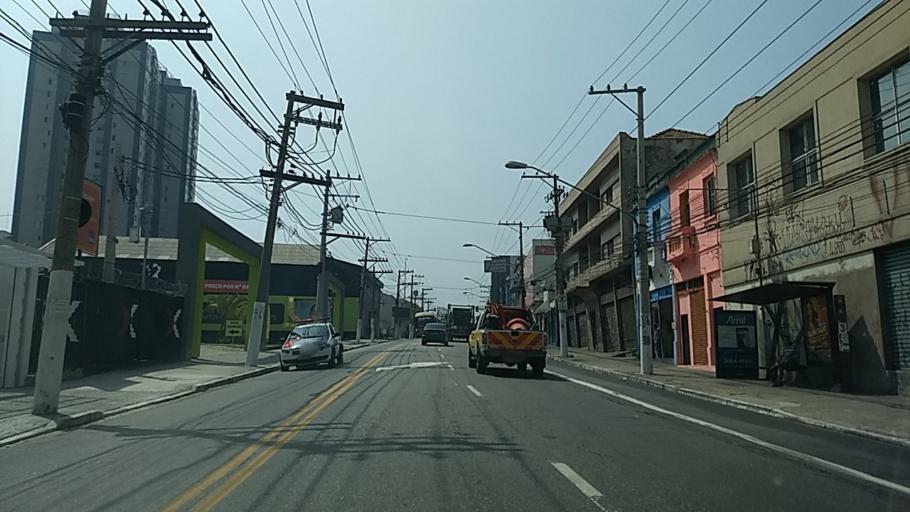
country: BR
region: Sao Paulo
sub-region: Sao Paulo
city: Sao Paulo
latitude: -23.5350
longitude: -46.5802
